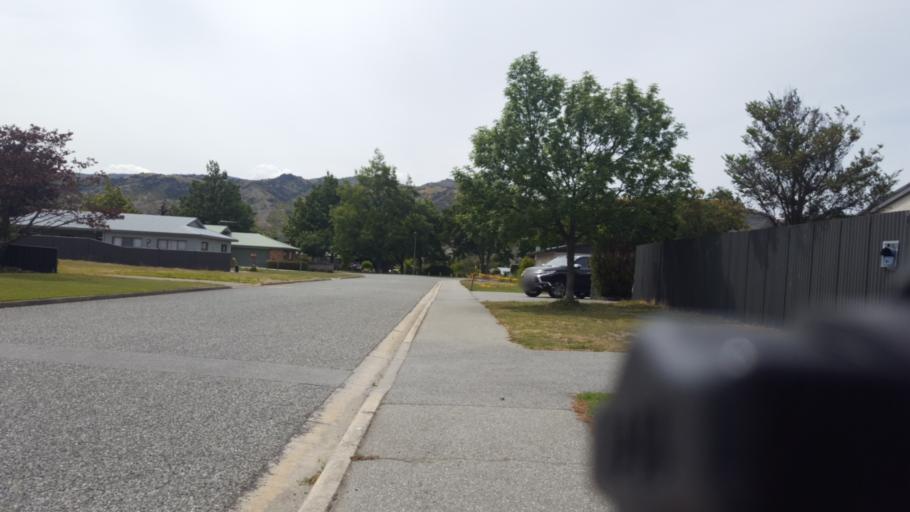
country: NZ
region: Otago
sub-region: Queenstown-Lakes District
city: Wanaka
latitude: -45.0422
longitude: 169.1980
